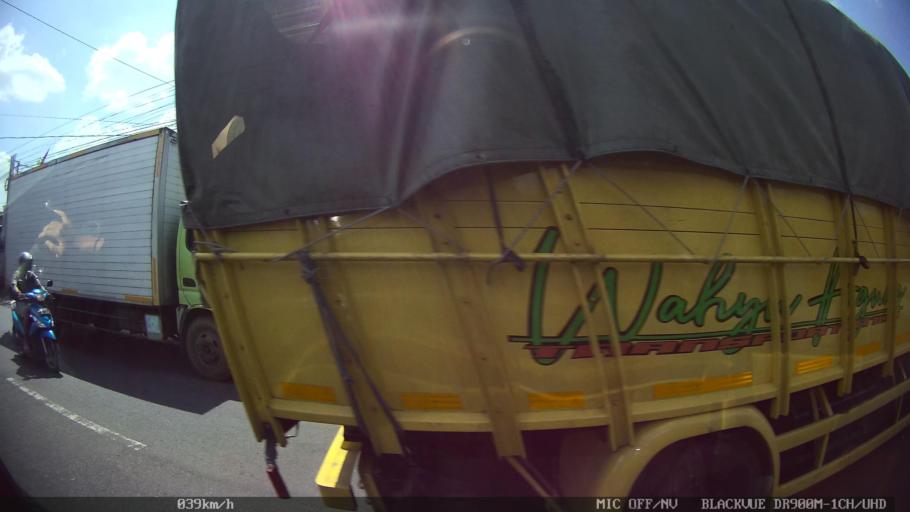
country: ID
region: Daerah Istimewa Yogyakarta
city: Sewon
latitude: -7.8451
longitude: 110.3911
